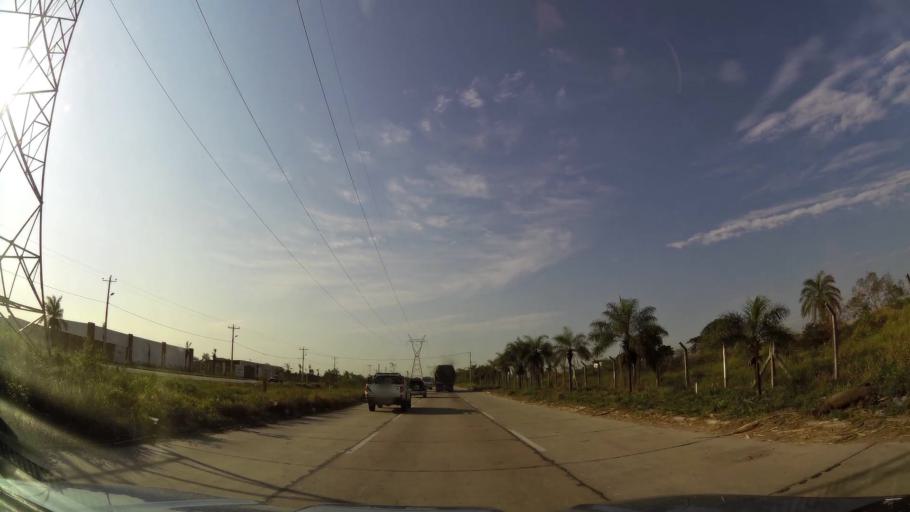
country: BO
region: Santa Cruz
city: Santa Cruz de la Sierra
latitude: -17.7018
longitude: -63.1335
